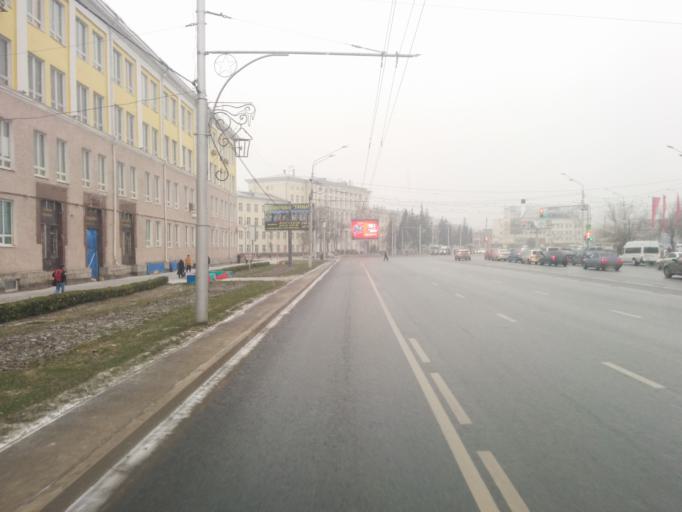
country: RU
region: Bashkortostan
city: Ufa
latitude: 54.7400
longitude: 55.9852
